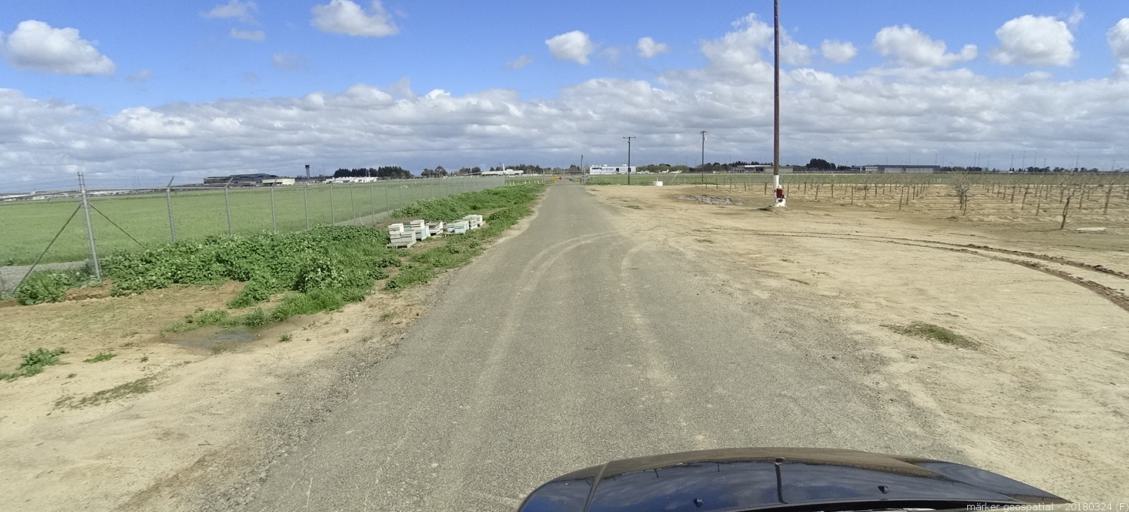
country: US
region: California
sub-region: Yolo County
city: West Sacramento
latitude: 38.6854
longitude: -121.6054
